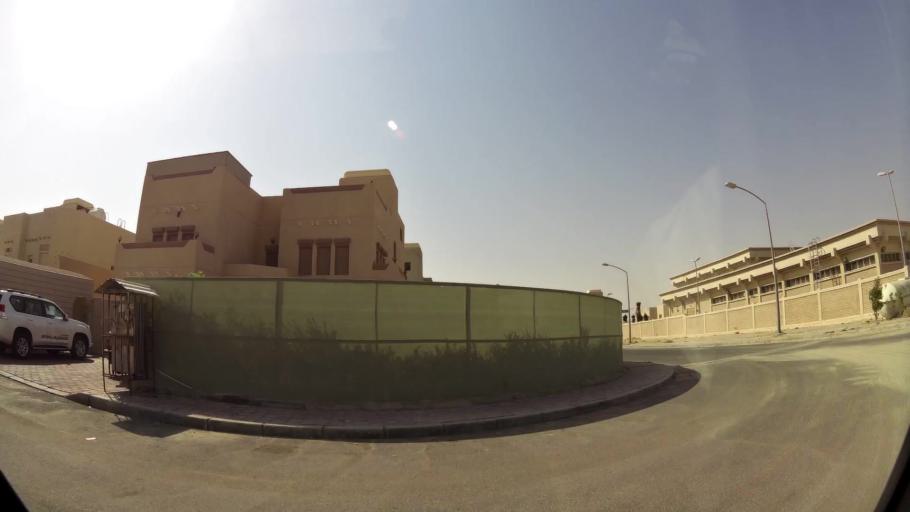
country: KW
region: Al Ahmadi
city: Al Wafrah
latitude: 28.8102
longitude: 48.0501
